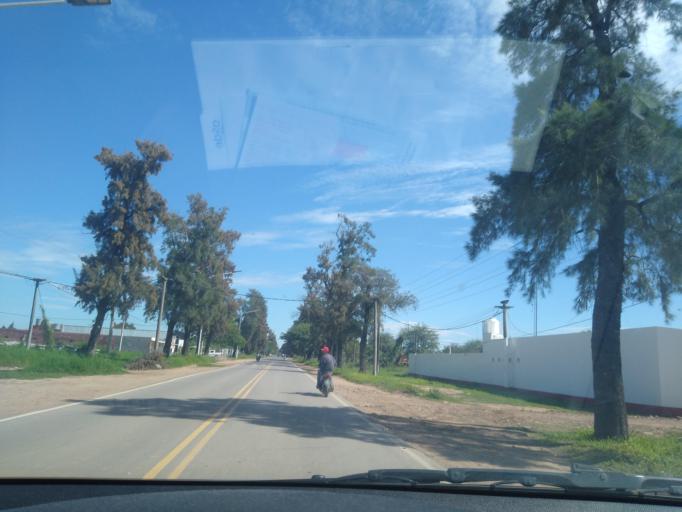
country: AR
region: Chaco
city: Presidencia Roque Saenz Pena
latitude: -26.7729
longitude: -60.4183
